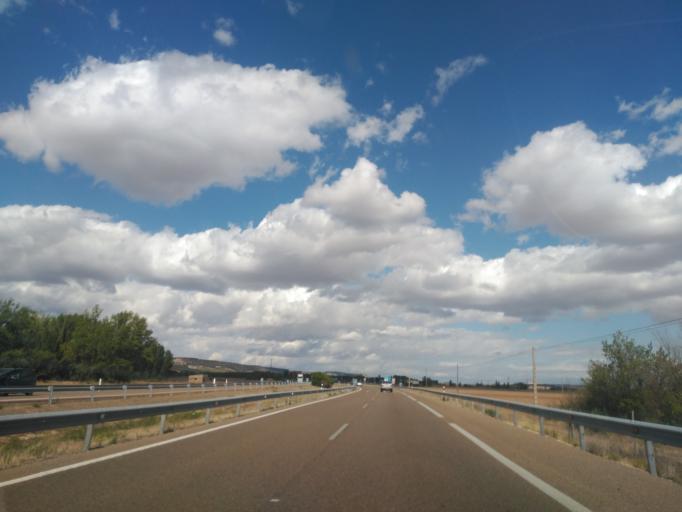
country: ES
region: Castille and Leon
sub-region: Provincia de Palencia
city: Cordovilla la Real
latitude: 42.0430
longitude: -4.2611
